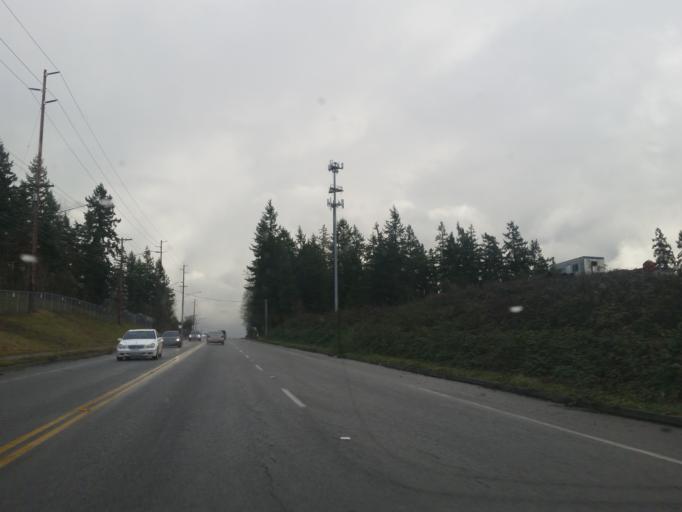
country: US
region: Washington
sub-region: Snohomish County
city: Brier
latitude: 47.7915
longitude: -122.2462
